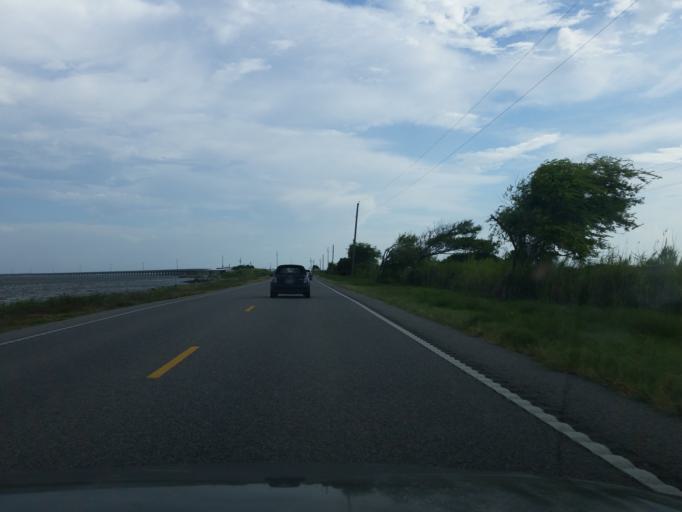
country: US
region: Alabama
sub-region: Mobile County
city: Dauphin Island
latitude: 30.3164
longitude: -88.1377
